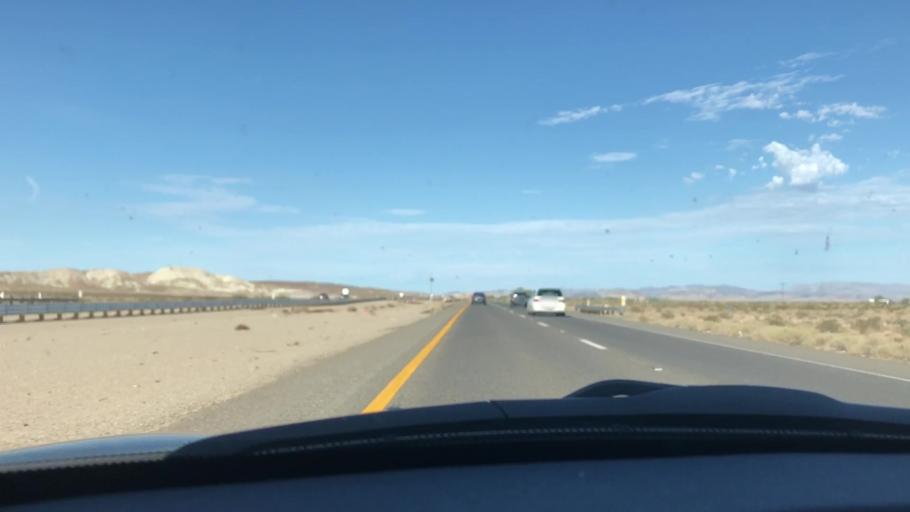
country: US
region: California
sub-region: San Bernardino County
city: Barstow
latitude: 34.9227
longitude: -116.7483
